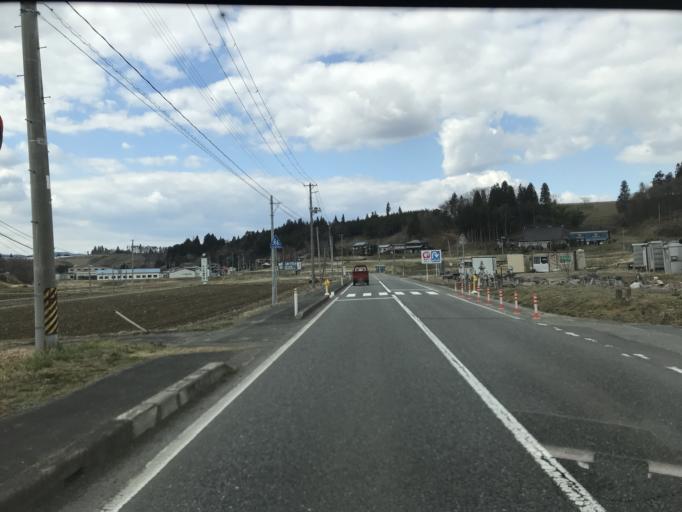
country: JP
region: Iwate
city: Ichinoseki
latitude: 38.8800
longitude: 141.3547
